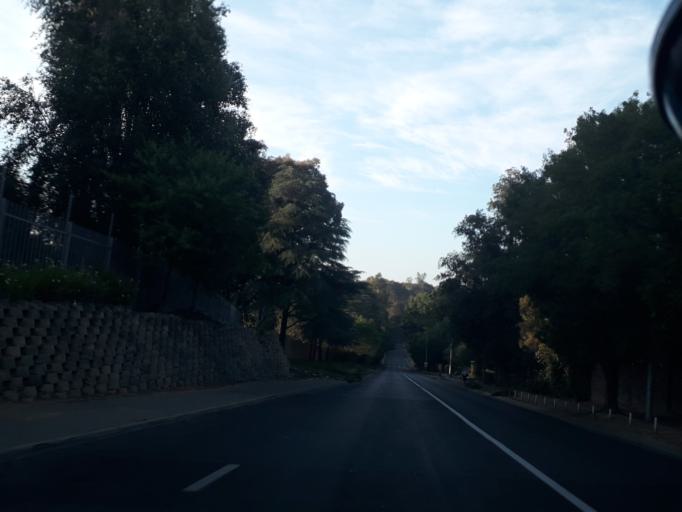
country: ZA
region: Gauteng
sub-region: City of Johannesburg Metropolitan Municipality
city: Diepsloot
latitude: -26.0548
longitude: 28.0047
